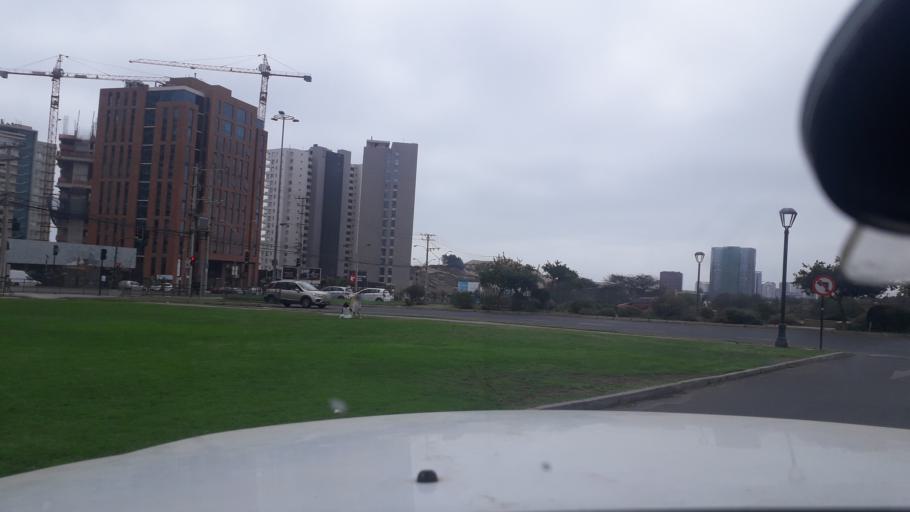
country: CL
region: Valparaiso
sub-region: Provincia de Valparaiso
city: Vina del Mar
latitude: -32.9494
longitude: -71.5444
